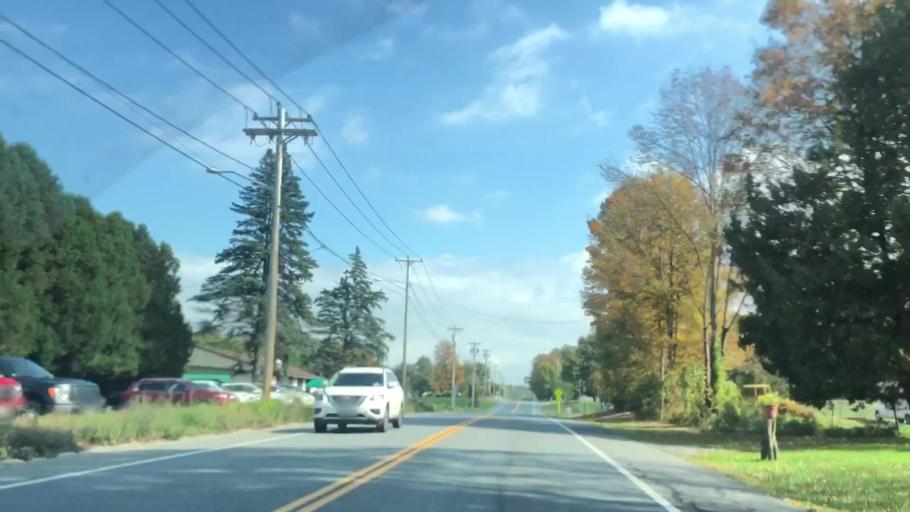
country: US
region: New York
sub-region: Warren County
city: Queensbury
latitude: 43.3968
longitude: -73.6310
